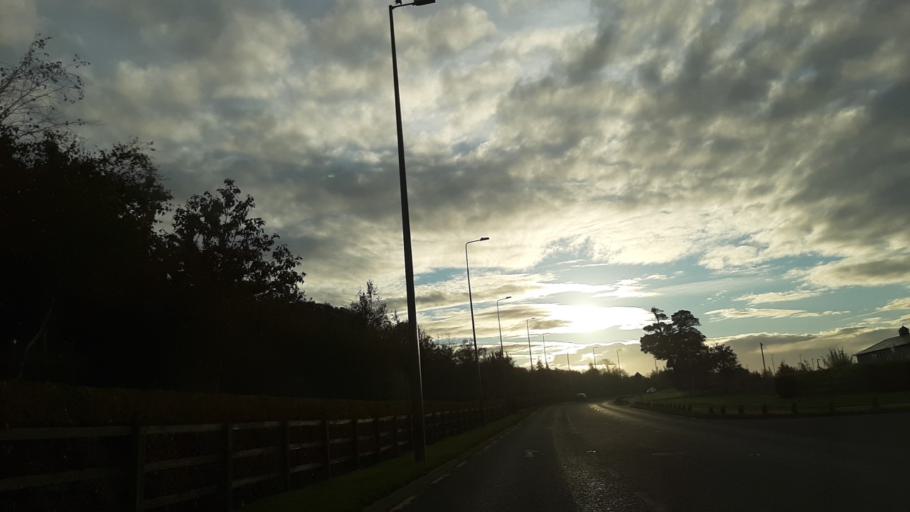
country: IE
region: Leinster
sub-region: Kildare
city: Athgarvan
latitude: 53.1699
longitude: -6.8432
